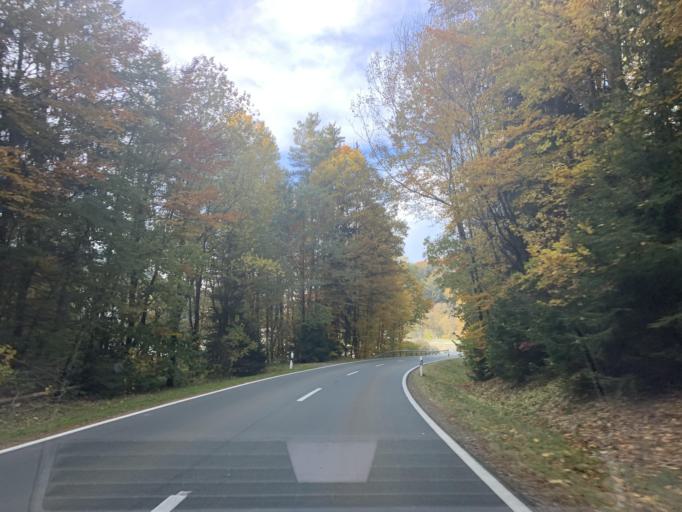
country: DE
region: Bavaria
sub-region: Upper Palatinate
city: Bach
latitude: 49.3895
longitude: 12.3949
